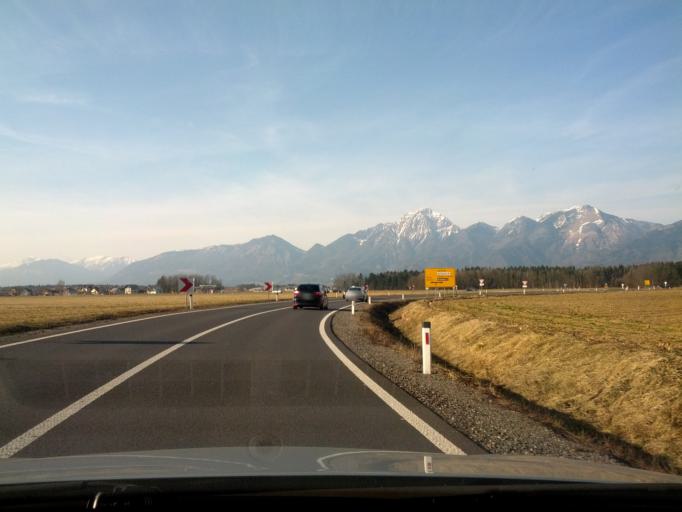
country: SI
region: Sencur
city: Sencur
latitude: 46.2339
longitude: 14.4319
